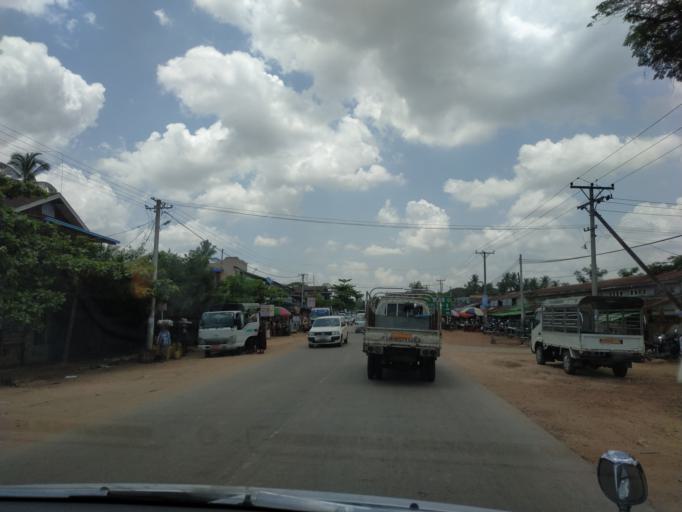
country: MM
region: Bago
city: Bago
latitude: 17.4747
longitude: 96.5260
